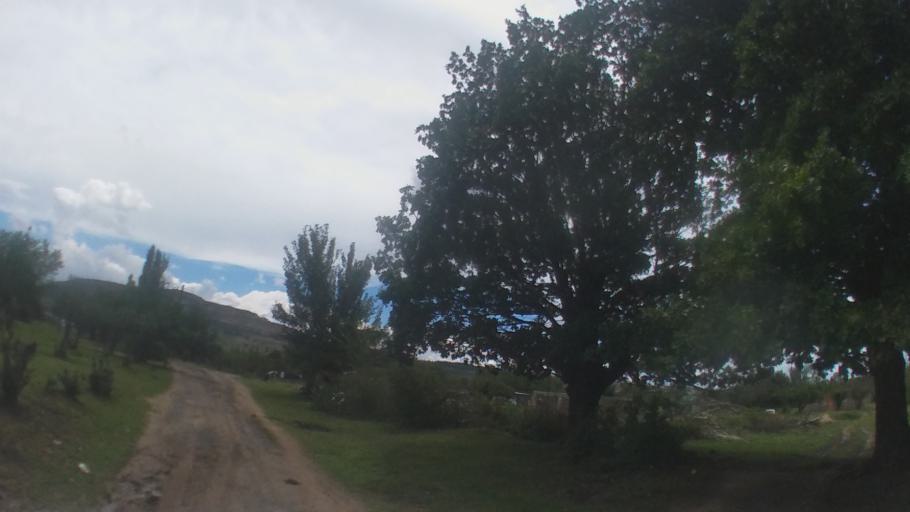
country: LS
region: Maseru
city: Nako
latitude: -29.6218
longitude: 27.5070
